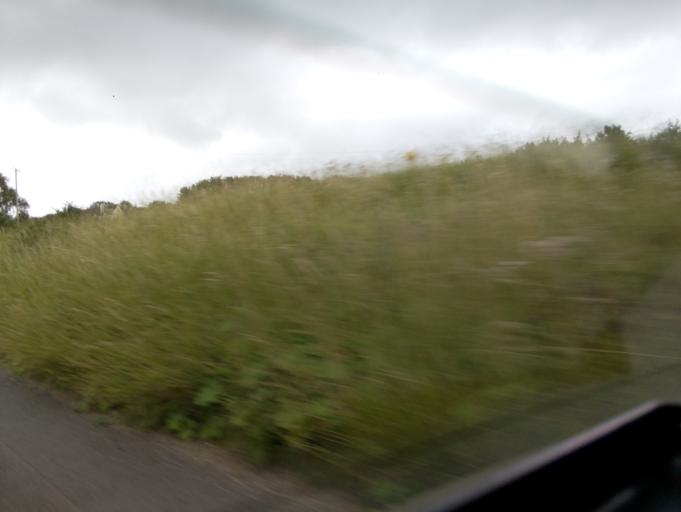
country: GB
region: England
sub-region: Gloucestershire
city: Painswick
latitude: 51.8152
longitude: -2.1493
